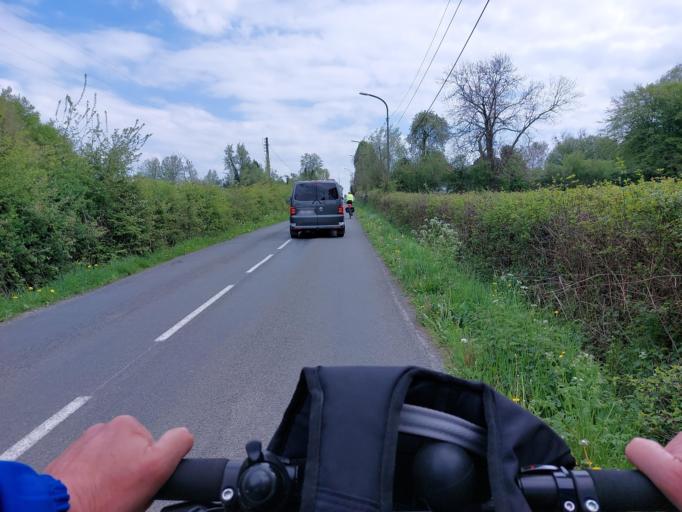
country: FR
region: Nord-Pas-de-Calais
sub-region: Departement du Nord
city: Hautmont
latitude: 50.2693
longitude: 3.8933
